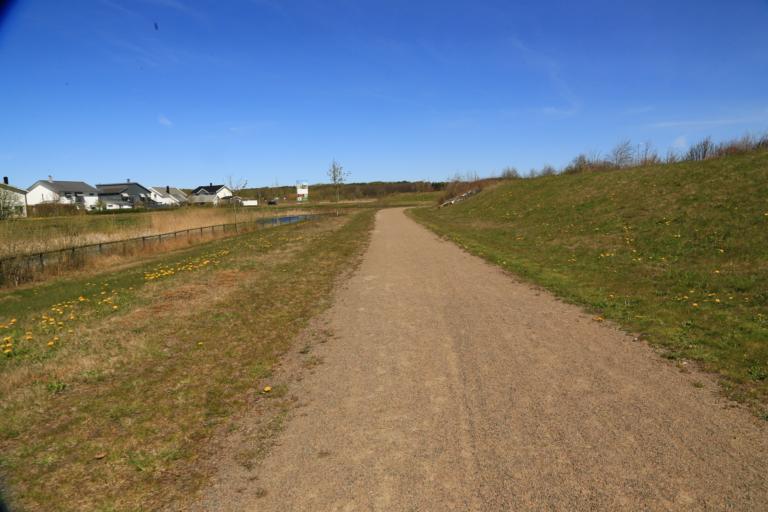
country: SE
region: Halland
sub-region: Varbergs Kommun
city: Traslovslage
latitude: 57.0846
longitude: 12.2833
